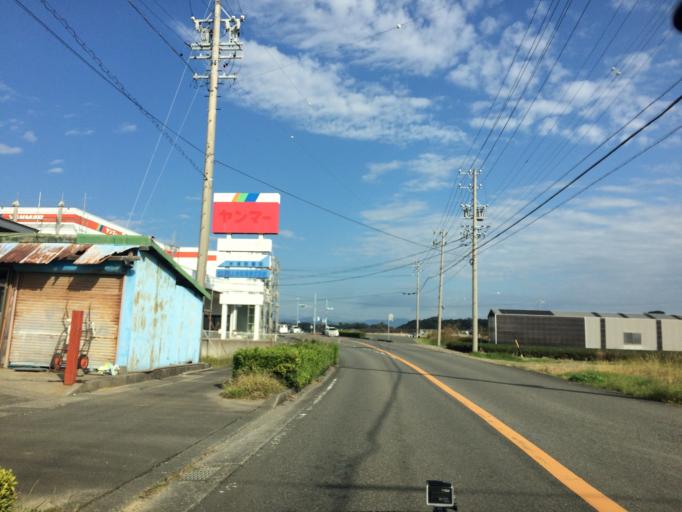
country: JP
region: Shizuoka
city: Shimada
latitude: 34.7631
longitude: 138.2389
